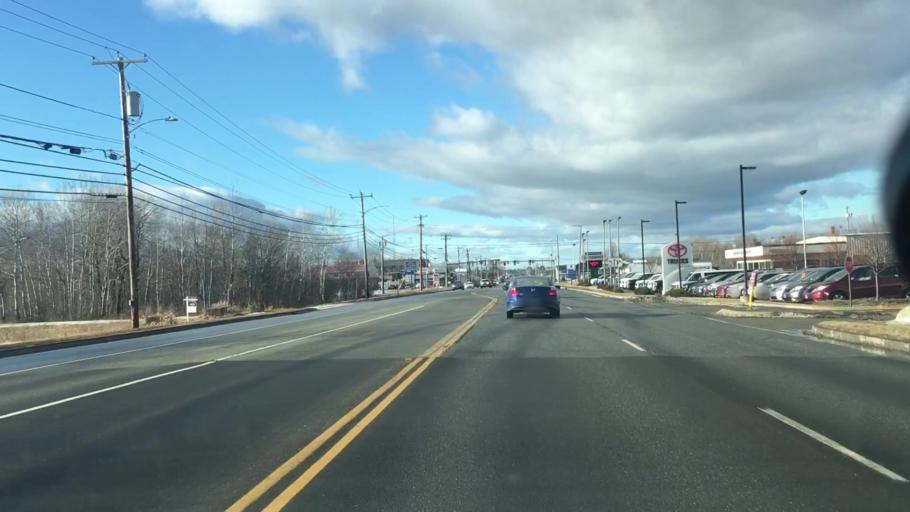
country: US
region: Maine
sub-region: Penobscot County
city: Brewer
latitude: 44.7770
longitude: -68.7345
